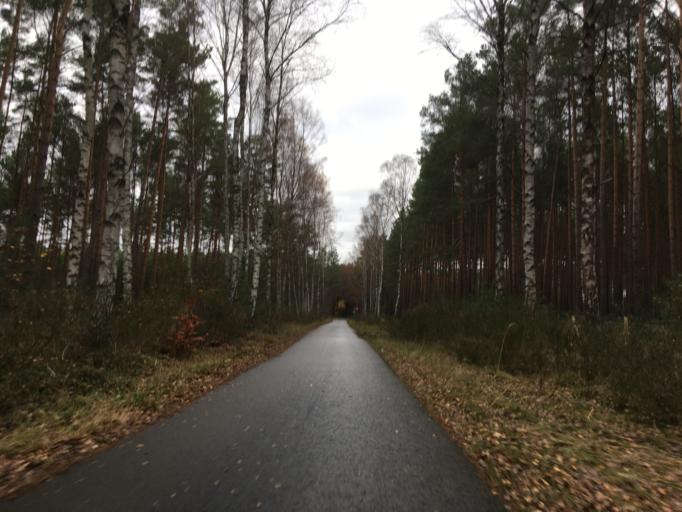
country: DE
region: Brandenburg
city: Jamlitz
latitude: 52.0558
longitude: 14.4814
